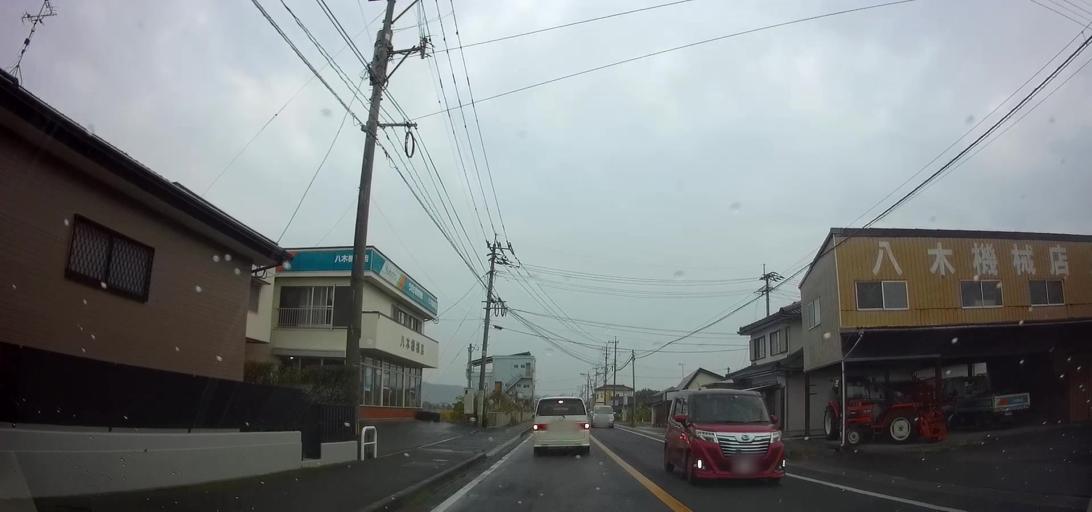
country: JP
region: Nagasaki
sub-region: Isahaya-shi
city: Isahaya
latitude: 32.8341
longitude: 130.1324
